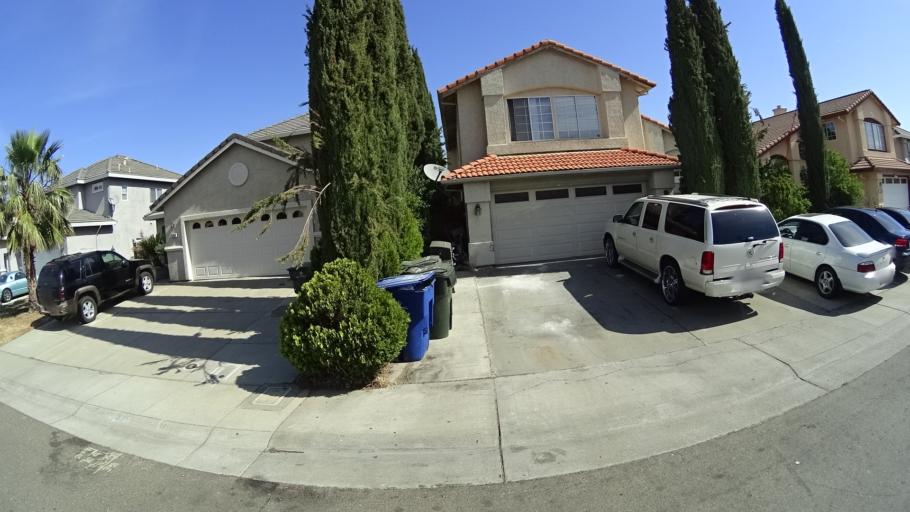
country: US
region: California
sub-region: Sacramento County
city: Florin
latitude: 38.5092
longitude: -121.4199
